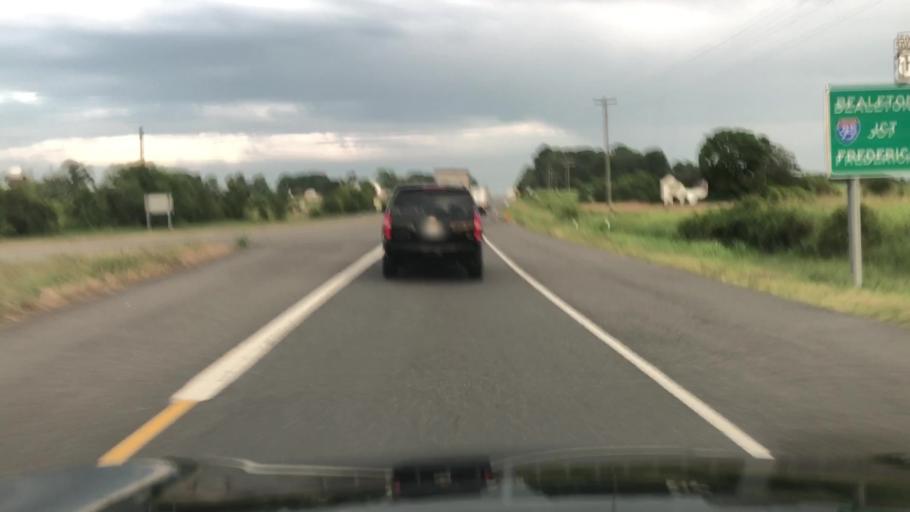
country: US
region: Virginia
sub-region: Fauquier County
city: Bealeton
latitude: 38.6099
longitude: -77.7895
